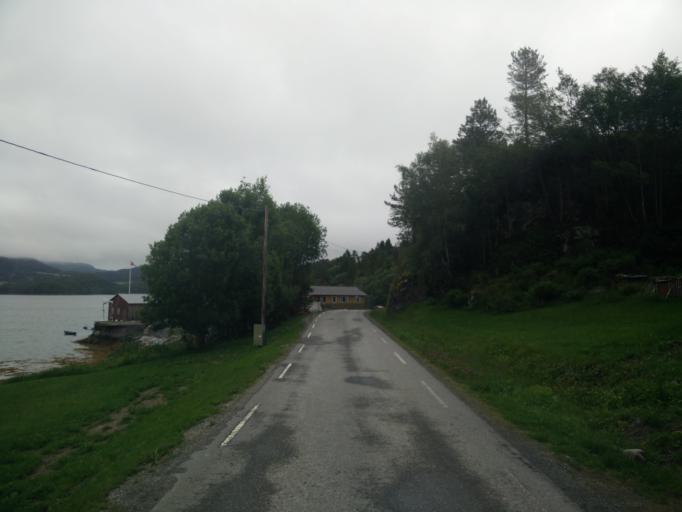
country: NO
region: More og Romsdal
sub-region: Kristiansund
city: Rensvik
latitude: 63.0187
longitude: 7.9533
